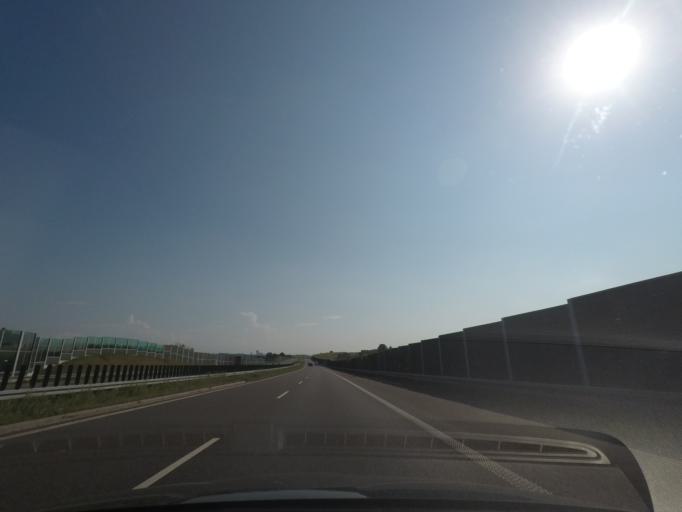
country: PL
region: Silesian Voivodeship
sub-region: Powiat rybnicki
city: Swierklany Dolne
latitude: 50.0075
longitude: 18.5822
